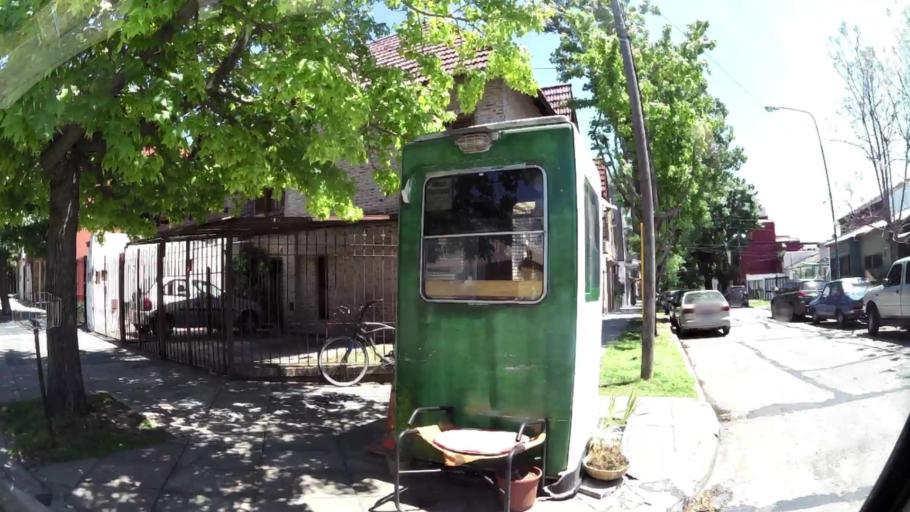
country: AR
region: Buenos Aires
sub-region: Partido de Vicente Lopez
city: Olivos
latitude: -34.5045
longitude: -58.4993
